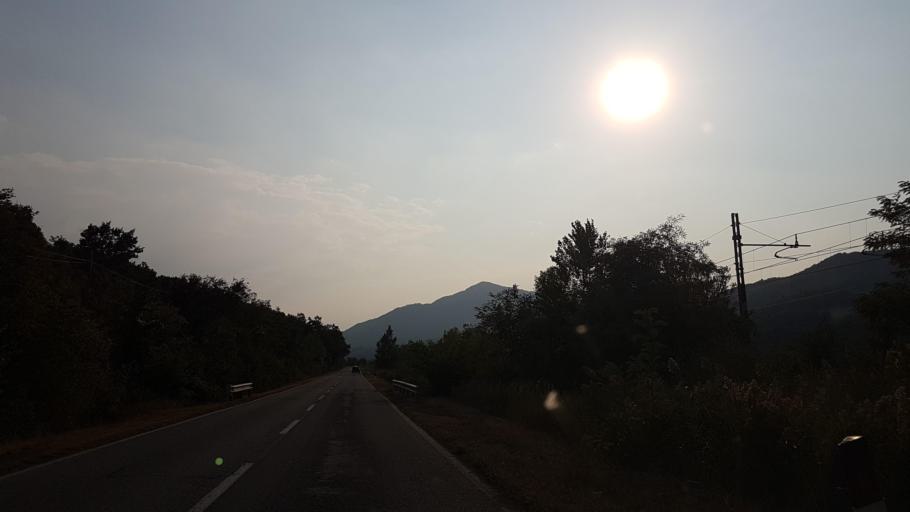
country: IT
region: Emilia-Romagna
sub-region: Provincia di Parma
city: Ramiola
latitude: 44.6600
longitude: 10.0627
